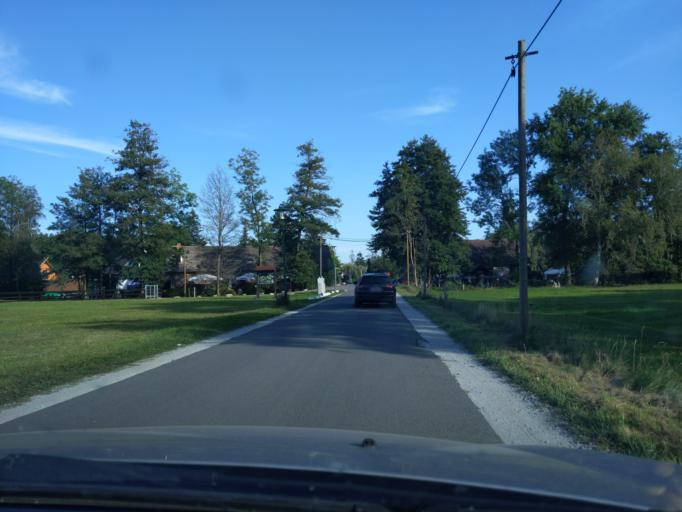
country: DE
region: Brandenburg
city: Straupitz
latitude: 51.8623
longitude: 14.0925
